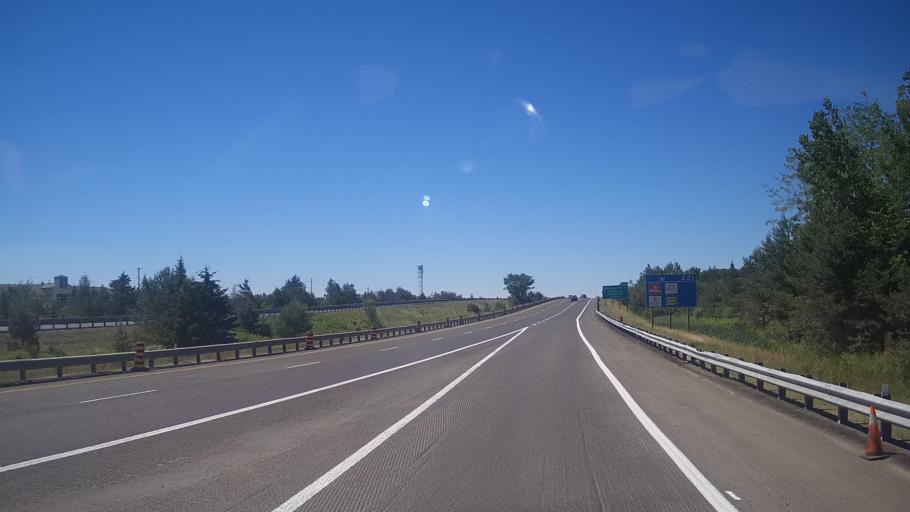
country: CA
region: Ontario
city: Huntsville
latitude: 45.3438
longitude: -79.2327
